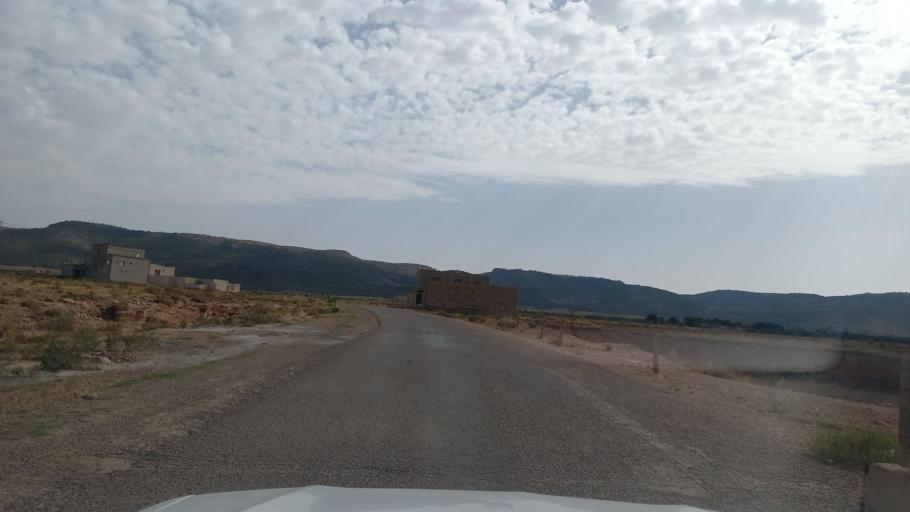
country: TN
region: Al Qasrayn
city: Kasserine
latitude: 35.3557
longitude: 8.8268
